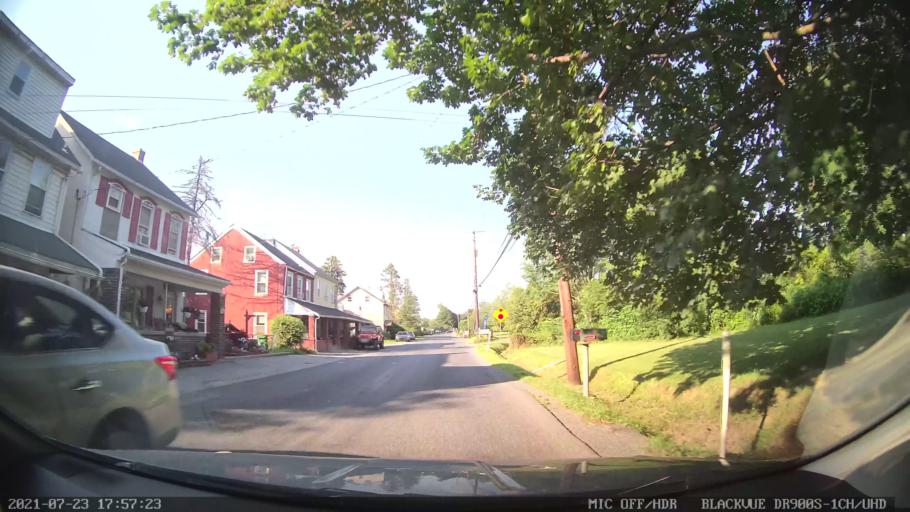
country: US
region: Pennsylvania
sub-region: Lehigh County
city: Macungie
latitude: 40.5175
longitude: -75.5468
